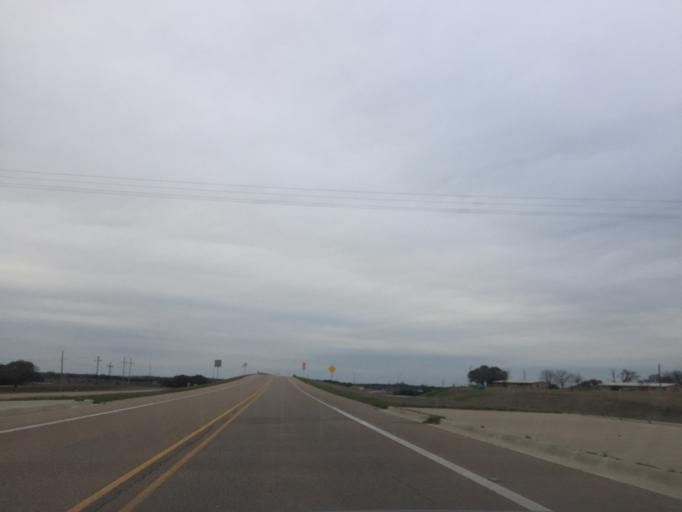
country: US
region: Texas
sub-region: Coryell County
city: Gatesville
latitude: 31.4815
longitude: -97.7307
